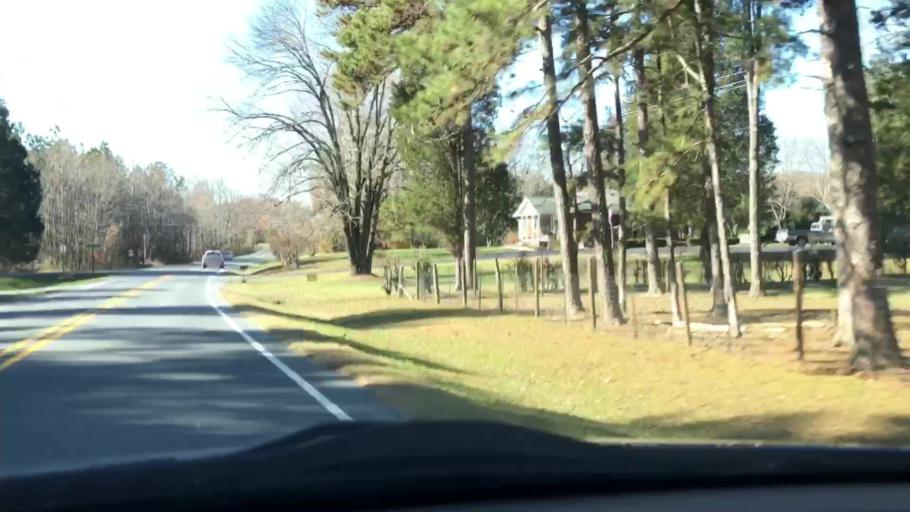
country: US
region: North Carolina
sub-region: Randolph County
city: Asheboro
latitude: 35.6766
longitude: -79.8771
